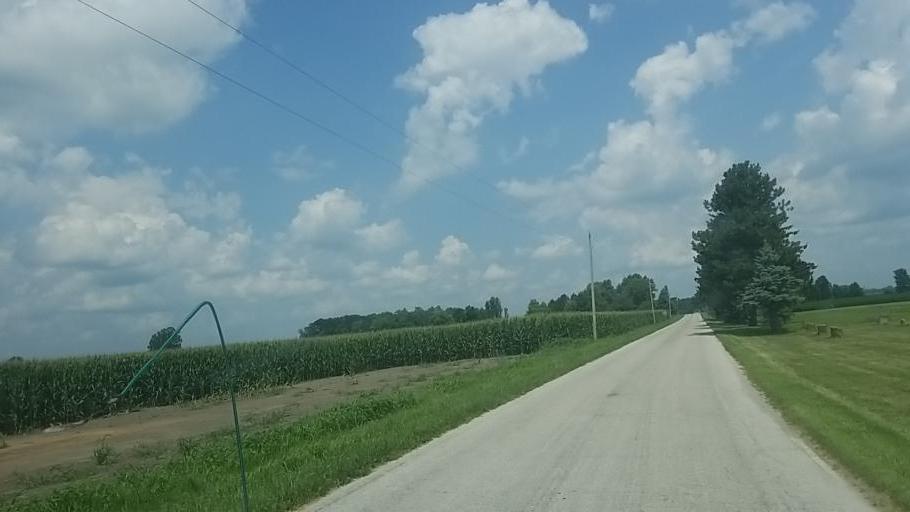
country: US
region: Ohio
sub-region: Crawford County
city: Bucyrus
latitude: 40.7783
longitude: -82.9979
